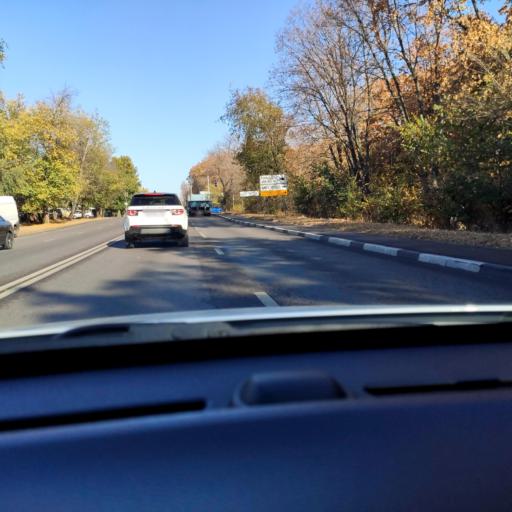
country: RU
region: Voronezj
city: Voronezh
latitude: 51.6672
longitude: 39.2712
